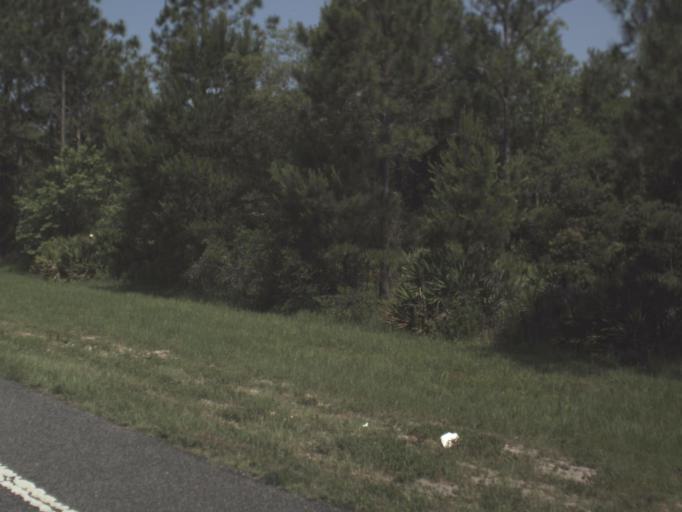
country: US
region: Florida
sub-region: Clay County
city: Green Cove Springs
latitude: 29.9831
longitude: -81.7628
